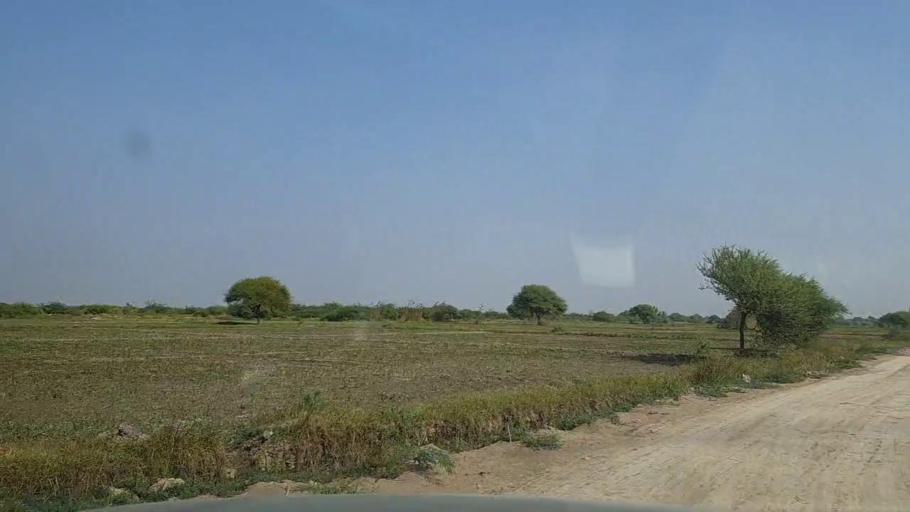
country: PK
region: Sindh
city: Mirpur Sakro
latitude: 24.5534
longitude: 67.5591
